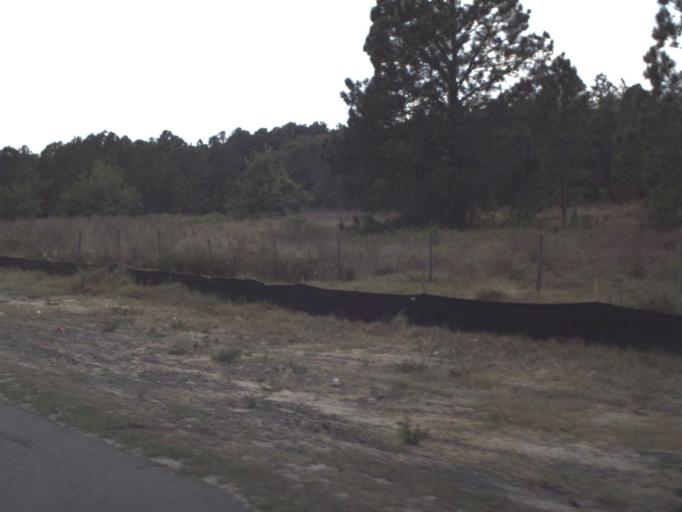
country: US
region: Florida
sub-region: Lake County
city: Clermont
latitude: 28.4775
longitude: -81.7153
